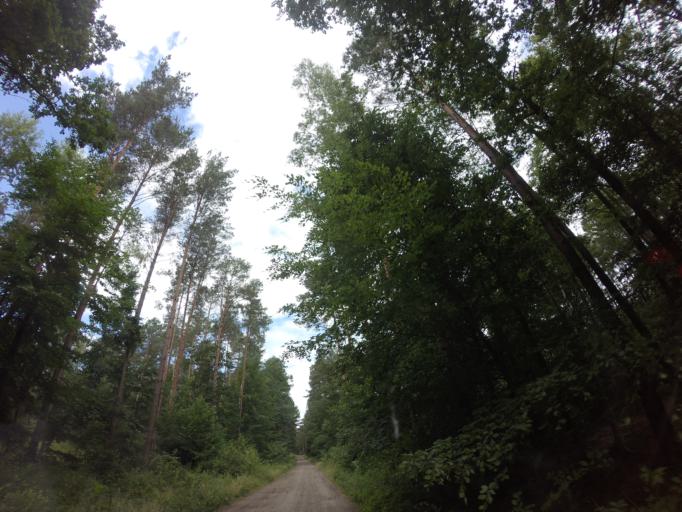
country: PL
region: West Pomeranian Voivodeship
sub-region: Powiat choszczenski
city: Bierzwnik
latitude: 53.0309
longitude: 15.6370
